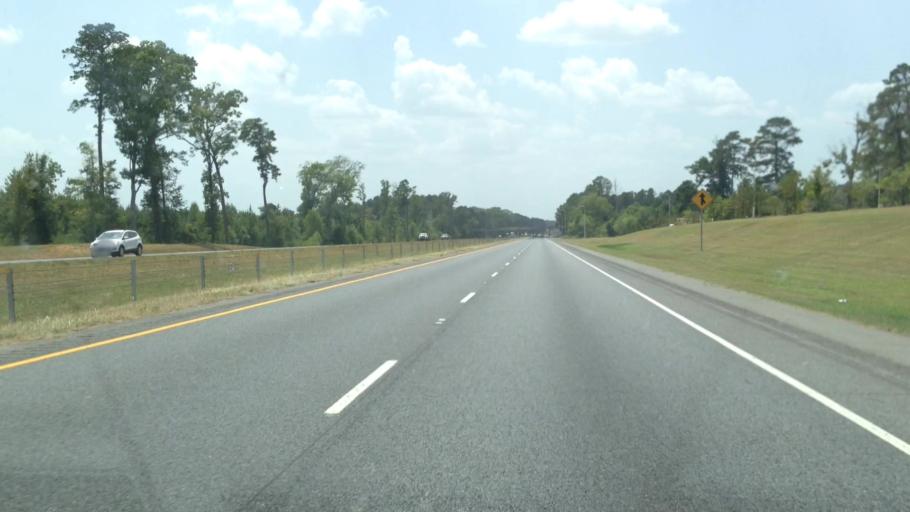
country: US
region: Louisiana
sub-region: Lincoln Parish
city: Ruston
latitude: 32.5289
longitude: -92.4470
